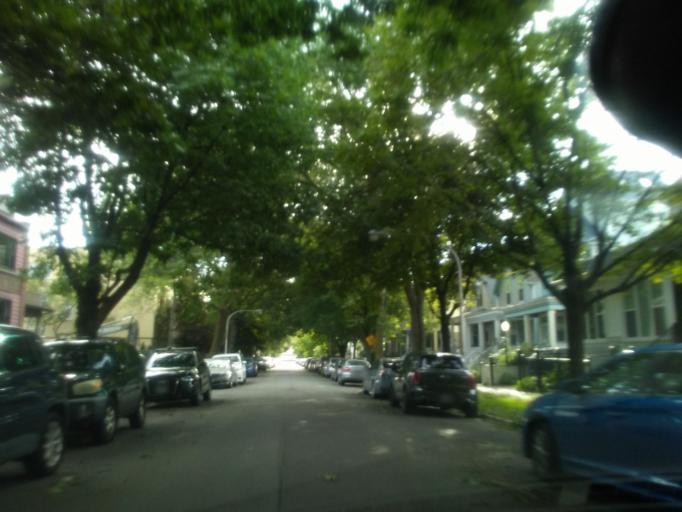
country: US
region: Illinois
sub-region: Cook County
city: Evanston
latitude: 41.9754
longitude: -87.6631
